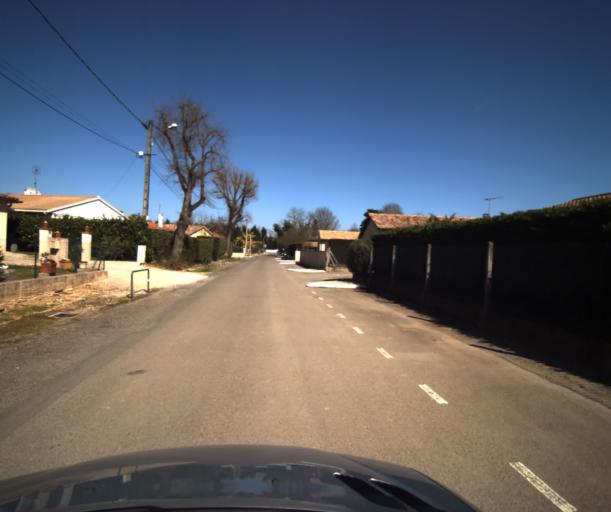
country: FR
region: Midi-Pyrenees
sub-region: Departement du Tarn-et-Garonne
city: Bressols
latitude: 43.9652
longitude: 1.3389
